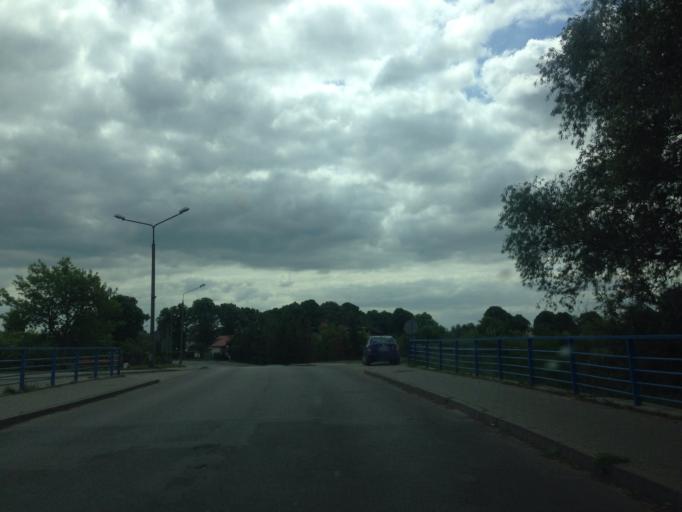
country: PL
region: Kujawsko-Pomorskie
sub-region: Powiat swiecki
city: Swiecie
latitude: 53.4040
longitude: 18.4510
